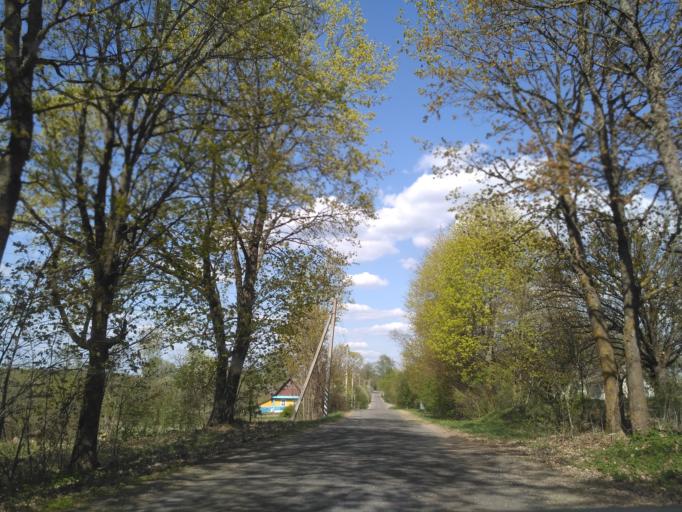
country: BY
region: Minsk
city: Narach
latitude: 54.9716
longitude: 26.6385
